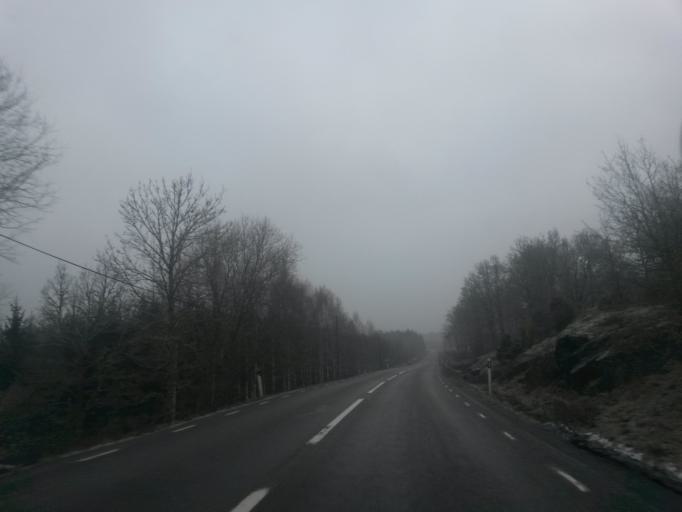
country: SE
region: Vaestra Goetaland
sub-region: Alingsas Kommun
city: Sollebrunn
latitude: 58.1761
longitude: 12.4173
